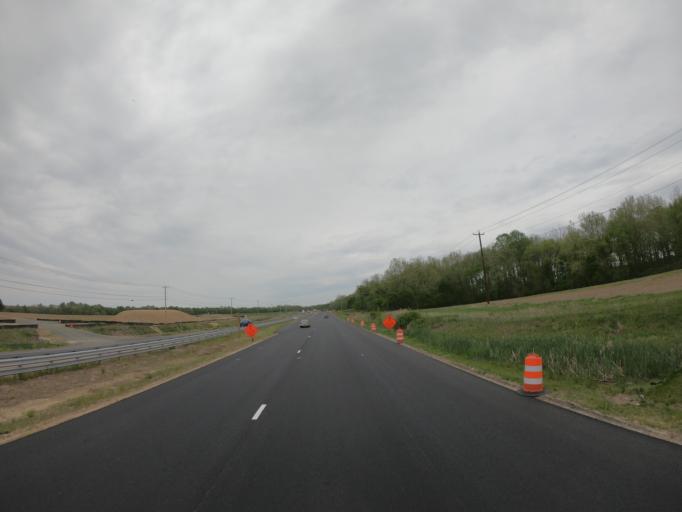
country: US
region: Maryland
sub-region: Caroline County
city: Ridgely
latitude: 38.9259
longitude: -75.9896
